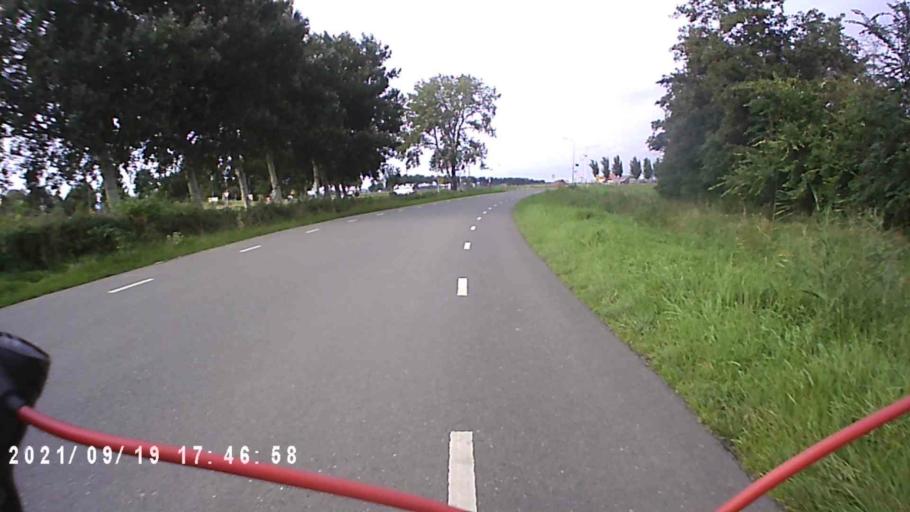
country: NL
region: Groningen
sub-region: Gemeente Delfzijl
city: Delfzijl
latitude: 53.2622
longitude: 6.9523
